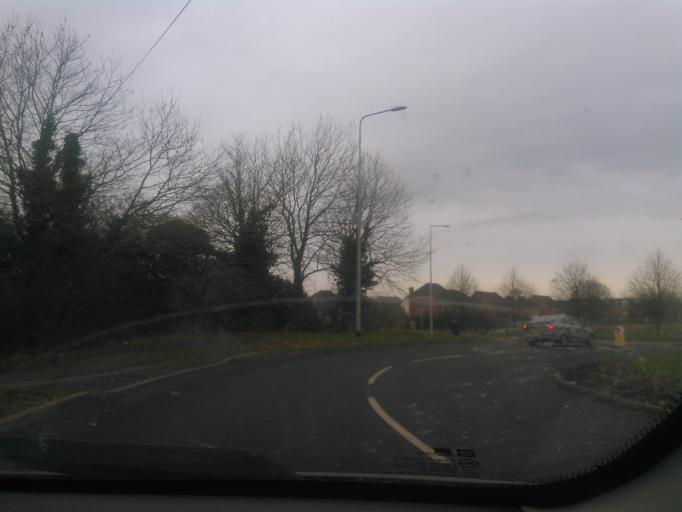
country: GB
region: England
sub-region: Telford and Wrekin
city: Oakengates
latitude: 52.7239
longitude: -2.4335
